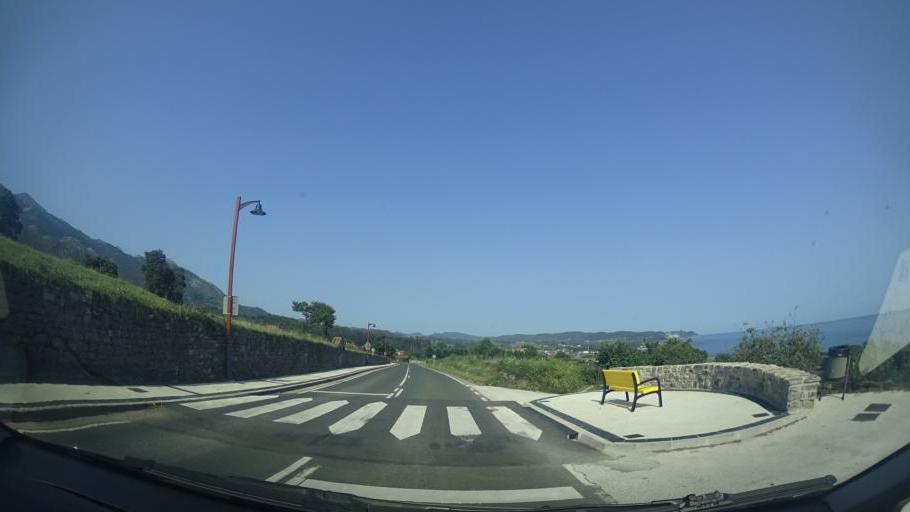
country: ES
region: Asturias
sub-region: Province of Asturias
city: Colunga
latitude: 43.4673
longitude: -5.2019
